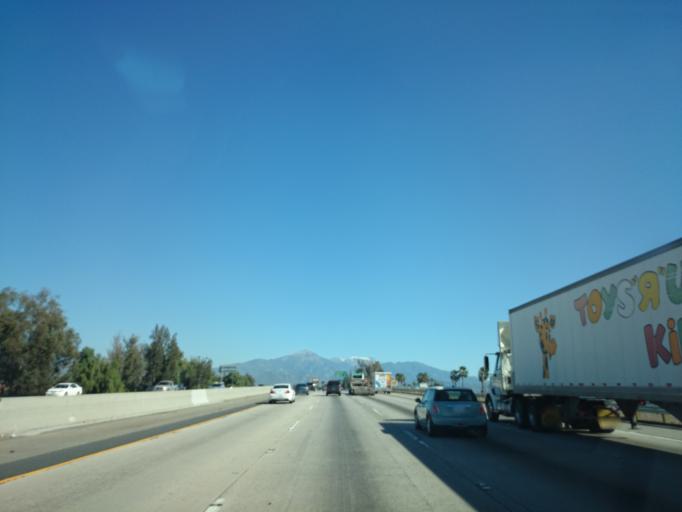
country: US
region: California
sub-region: San Bernardino County
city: Loma Linda
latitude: 34.0640
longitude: -117.2638
